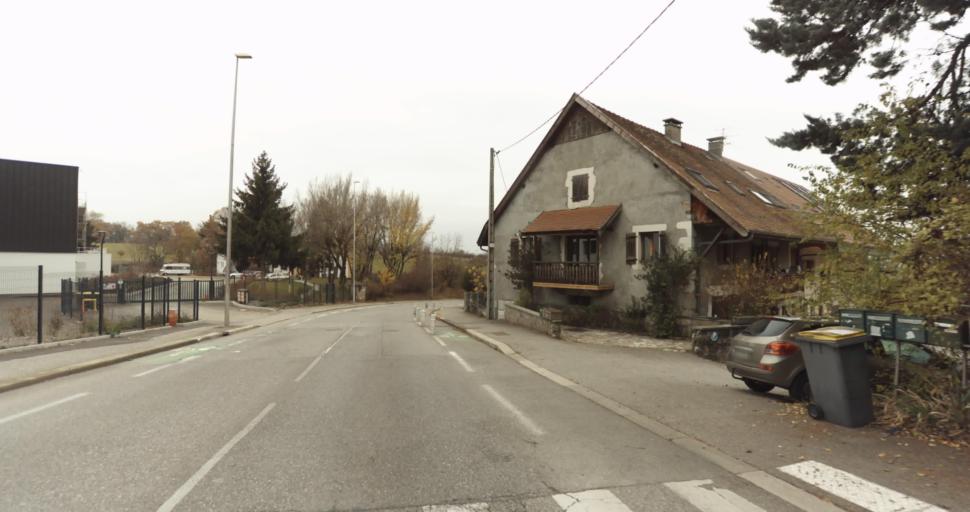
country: FR
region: Rhone-Alpes
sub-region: Departement de la Haute-Savoie
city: Cran-Gevrier
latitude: 45.8955
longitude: 6.1015
